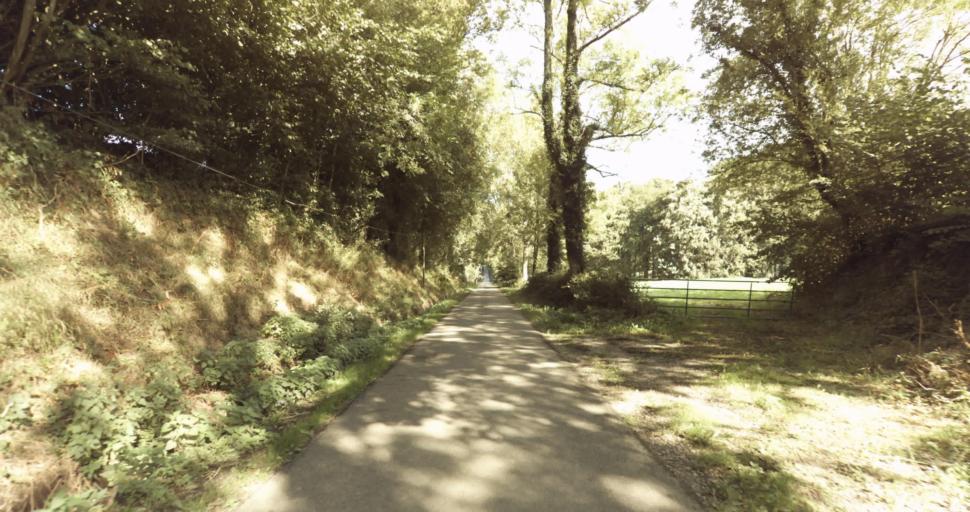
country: FR
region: Lower Normandy
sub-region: Departement de l'Orne
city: Gace
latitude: 48.8084
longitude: 0.2265
